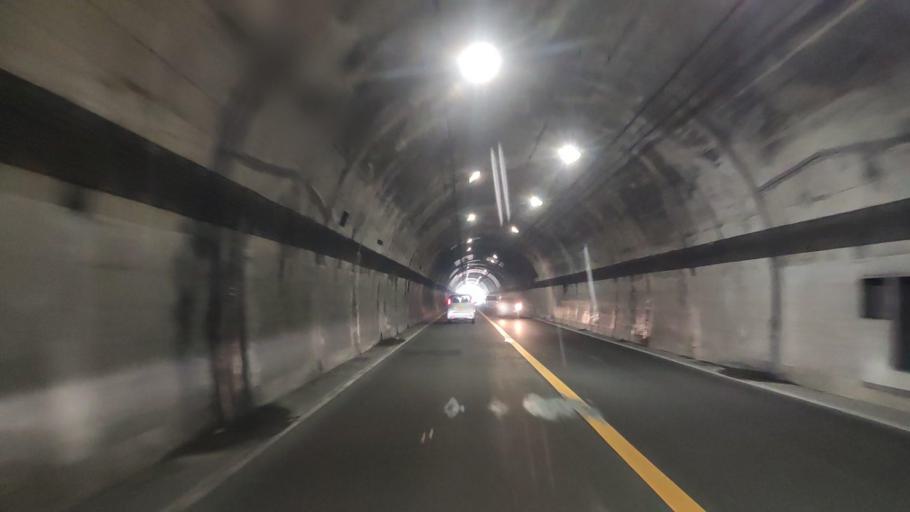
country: JP
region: Wakayama
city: Shingu
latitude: 33.5752
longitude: 135.9178
